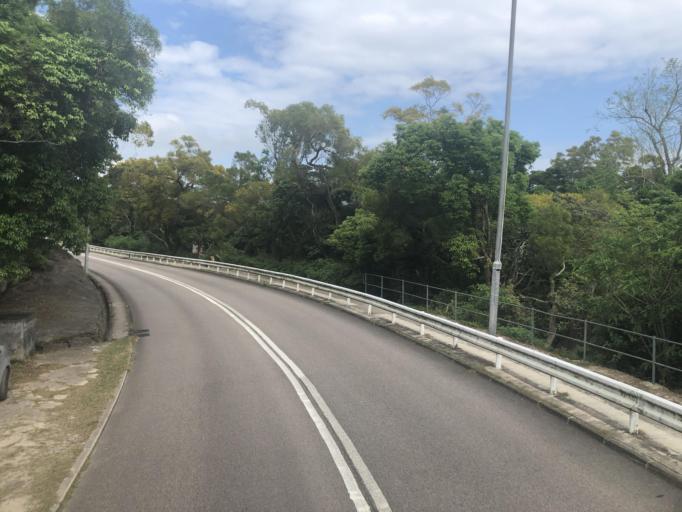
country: HK
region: Sai Kung
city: Sai Kung
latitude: 22.3865
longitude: 114.3047
